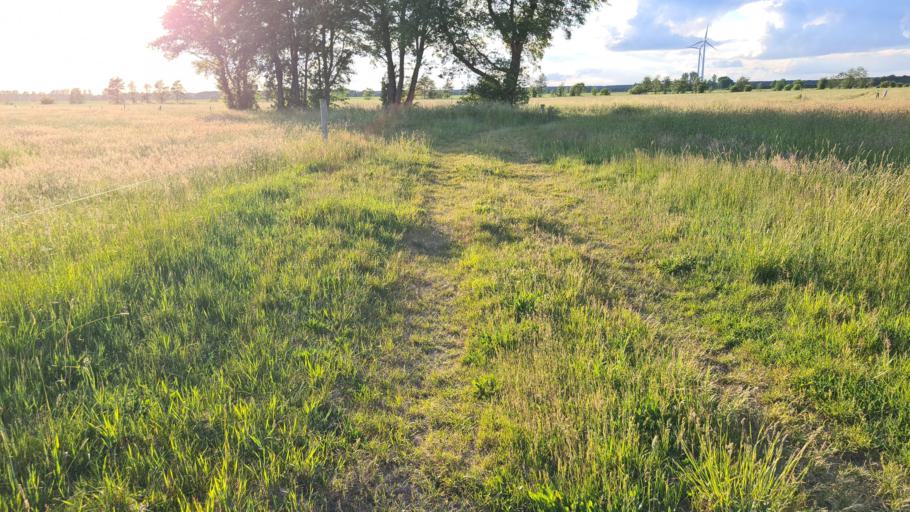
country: DE
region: Brandenburg
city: Schilda
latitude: 51.6156
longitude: 13.3492
